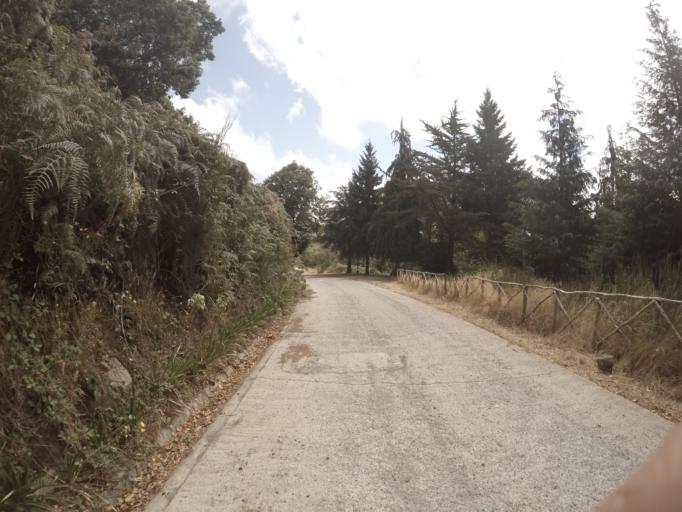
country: PT
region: Madeira
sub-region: Camara de Lobos
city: Curral das Freiras
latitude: 32.7086
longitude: -17.0109
